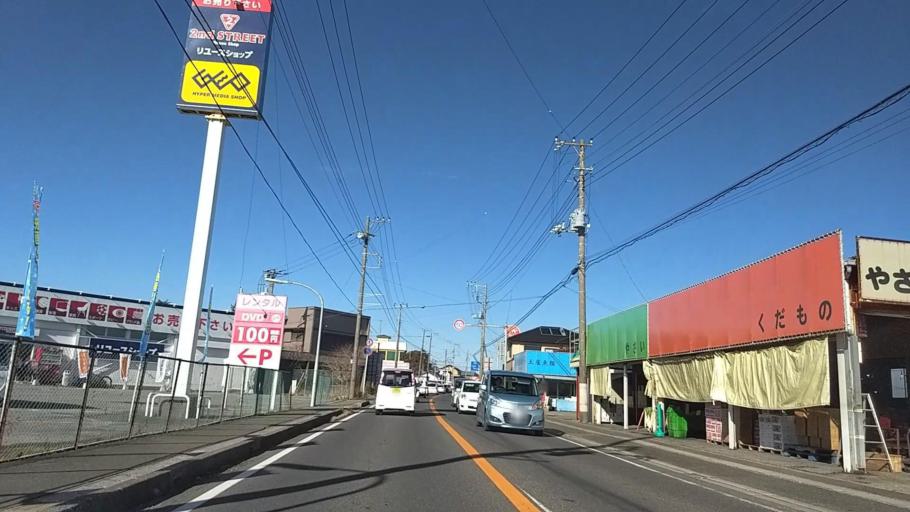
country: JP
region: Chiba
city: Ohara
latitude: 35.2589
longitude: 140.3935
